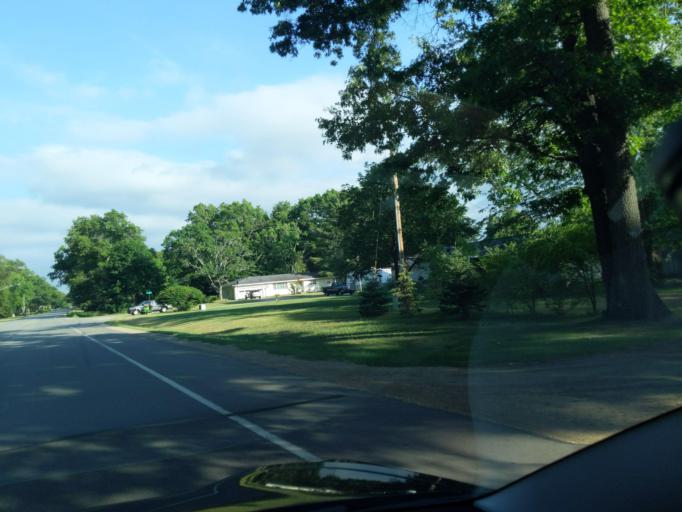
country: US
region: Michigan
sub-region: Muskegon County
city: Whitehall
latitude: 43.3981
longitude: -86.3054
